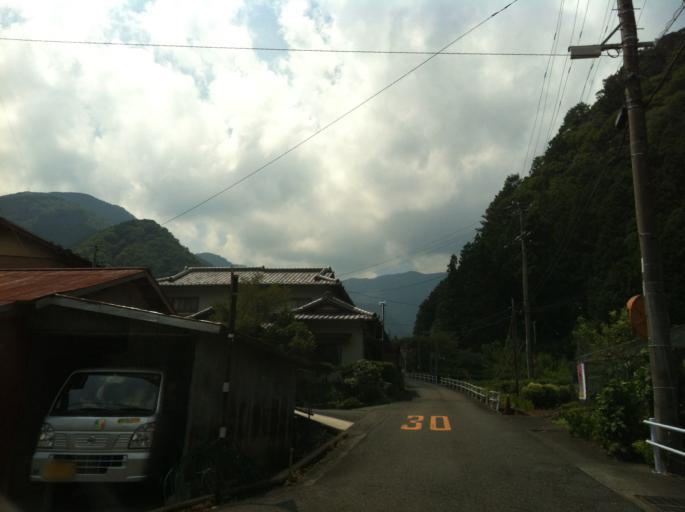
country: JP
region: Shizuoka
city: Fujinomiya
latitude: 35.2810
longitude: 138.3330
